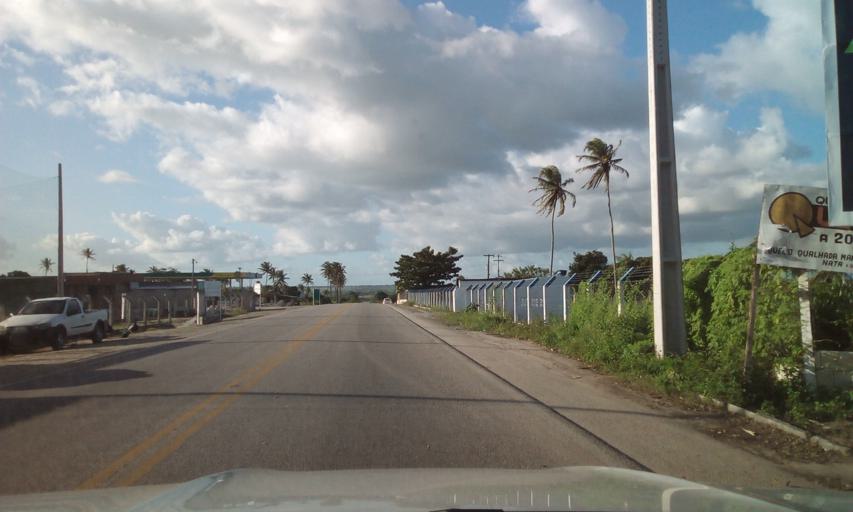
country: BR
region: Paraiba
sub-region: Pilar
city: Pilar
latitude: -7.1735
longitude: -35.2285
